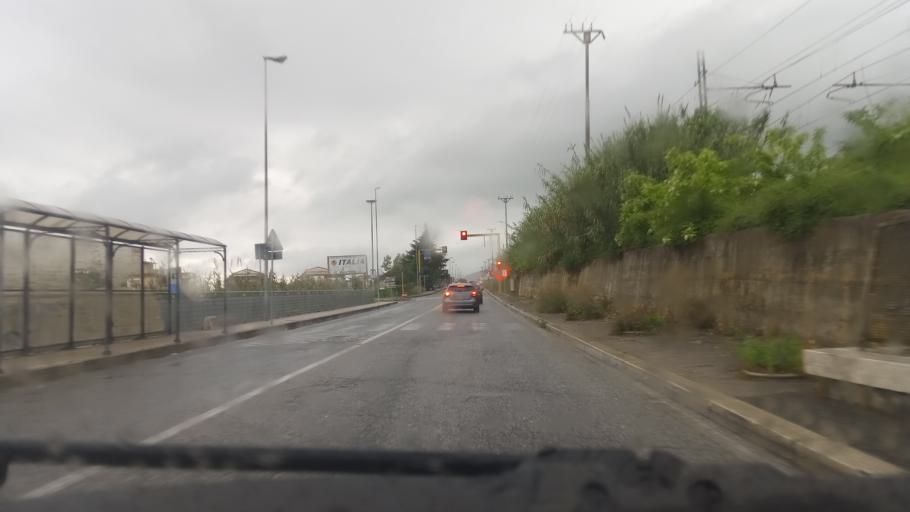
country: IT
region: Latium
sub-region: Provincia di Latina
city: Formia
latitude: 41.2635
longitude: 13.6664
